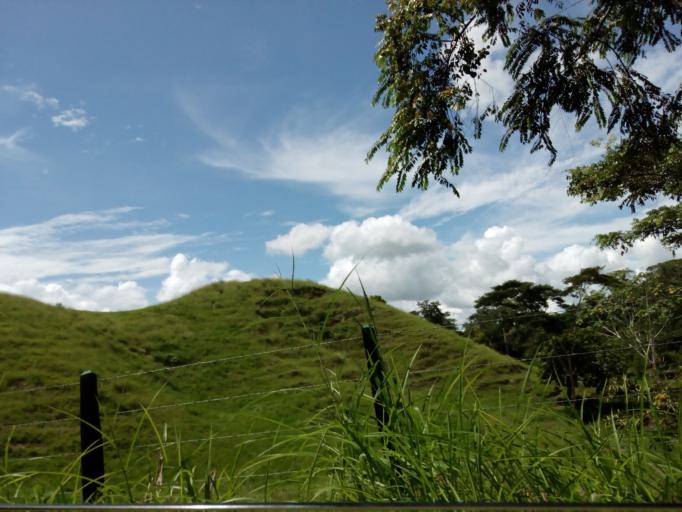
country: CO
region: Boyaca
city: Puerto Boyaca
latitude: 5.9589
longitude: -74.4660
